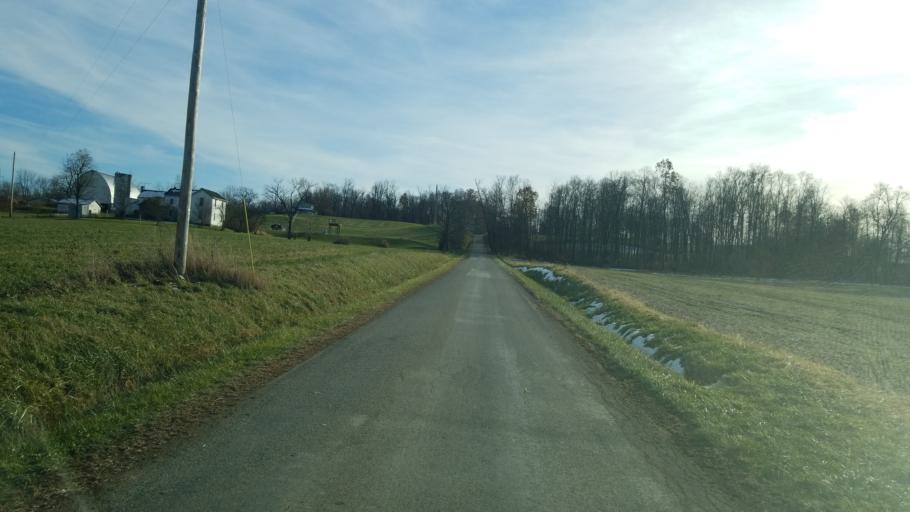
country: US
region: Ohio
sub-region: Ashland County
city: Ashland
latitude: 40.8151
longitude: -82.2277
